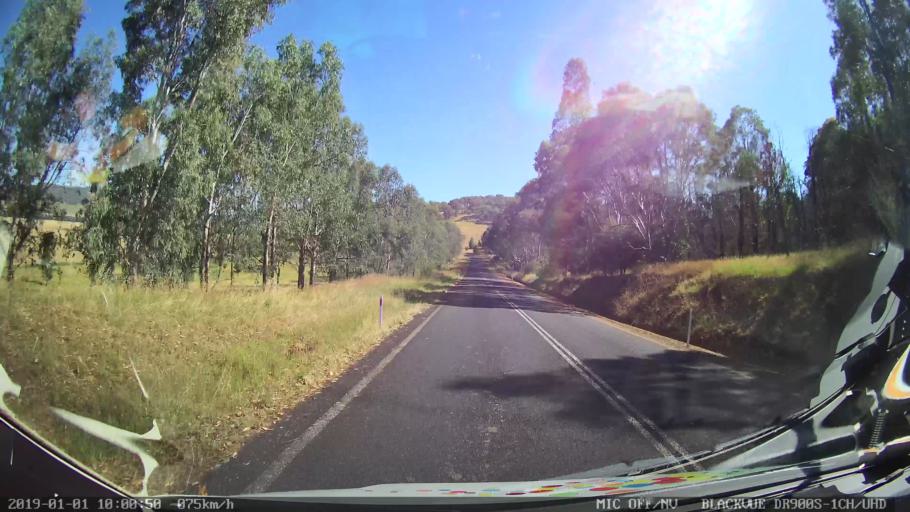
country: AU
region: New South Wales
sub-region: Snowy River
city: Jindabyne
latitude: -36.1979
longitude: 148.1027
